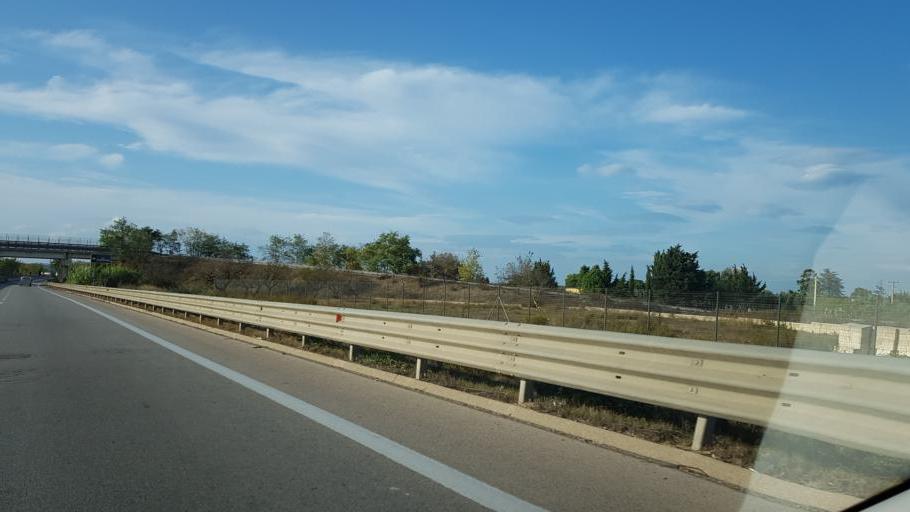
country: IT
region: Apulia
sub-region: Provincia di Brindisi
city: Francavilla Fontana
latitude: 40.5414
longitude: 17.6032
